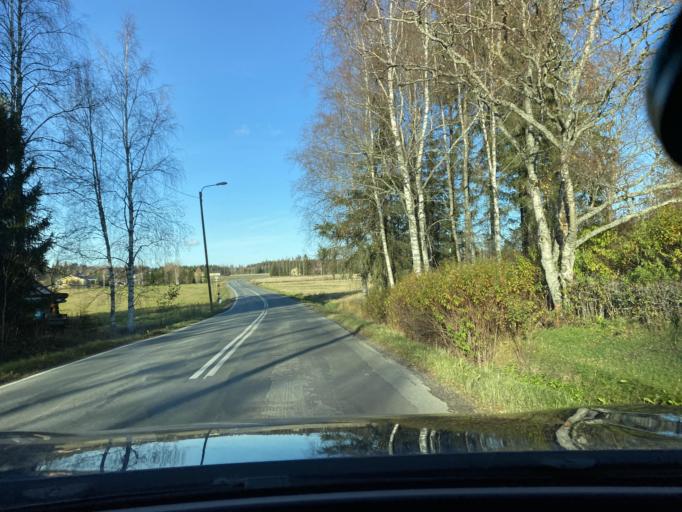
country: FI
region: Haeme
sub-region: Forssa
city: Tammela
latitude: 60.8298
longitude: 23.8407
